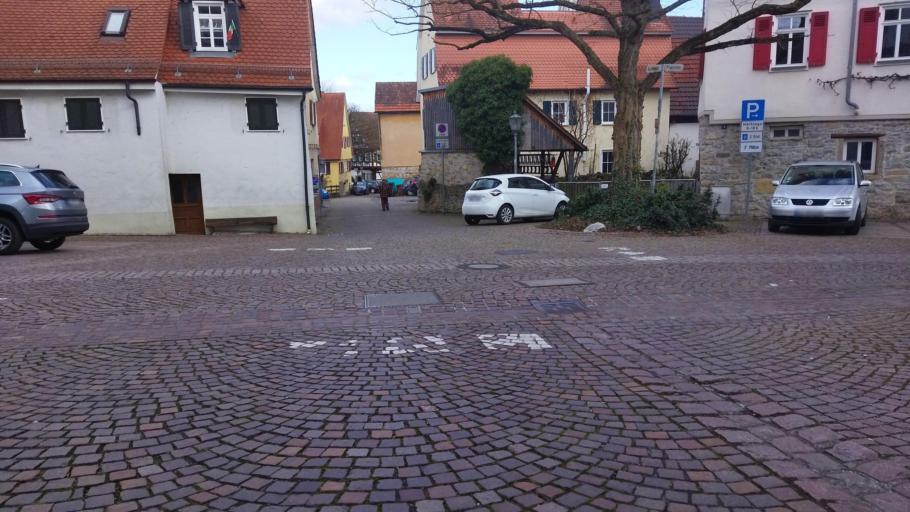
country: DE
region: Baden-Wuerttemberg
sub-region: Regierungsbezirk Stuttgart
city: Bietigheim-Bissingen
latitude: 48.9606
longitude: 9.1253
